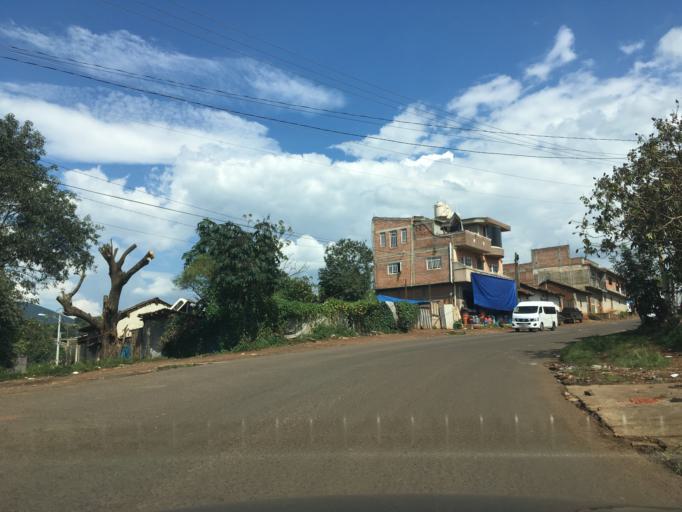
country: MX
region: Michoacan
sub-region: Los Reyes
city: J. Jesus Diaz Tzirio
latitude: 19.8461
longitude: -102.4665
